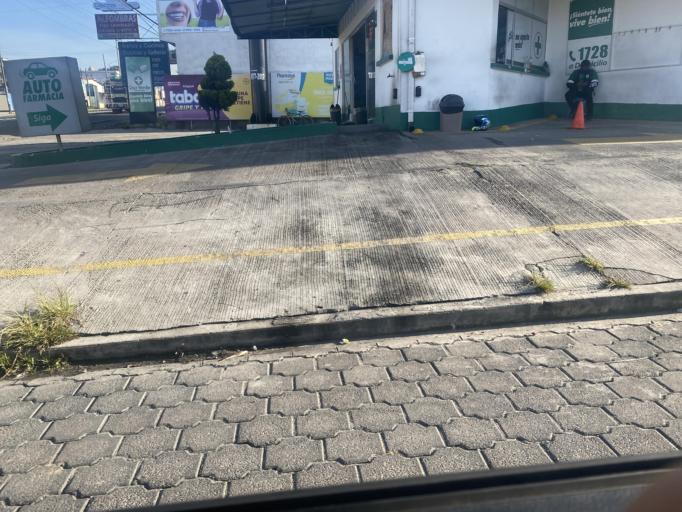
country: GT
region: Quetzaltenango
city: Quetzaltenango
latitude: 14.8559
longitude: -91.5215
